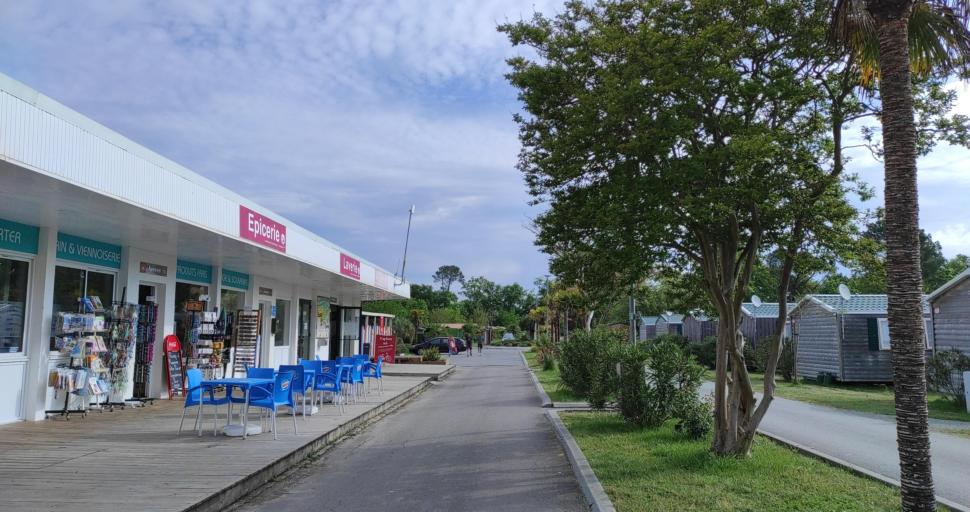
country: FR
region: Aquitaine
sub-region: Departement de la Gironde
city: Lanton
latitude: 44.7040
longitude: -1.0489
